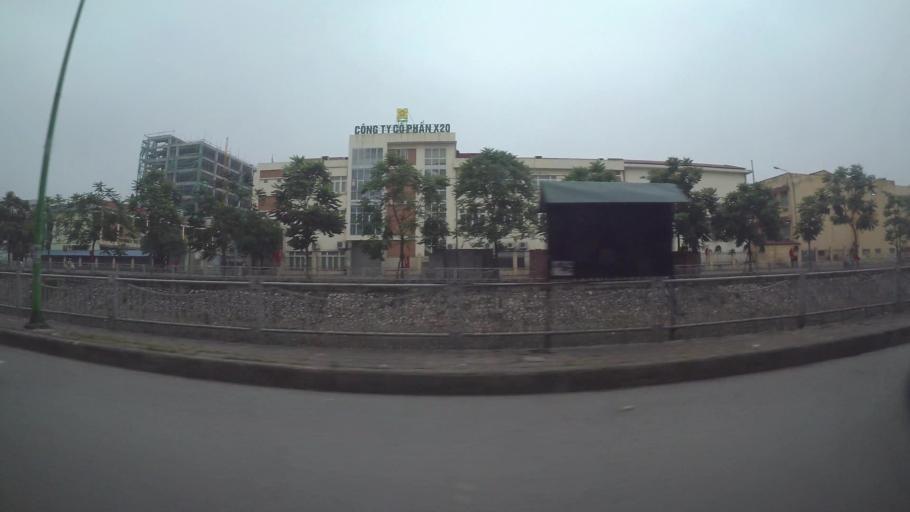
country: VN
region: Ha Noi
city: Hai BaTrung
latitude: 20.9907
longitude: 105.8369
